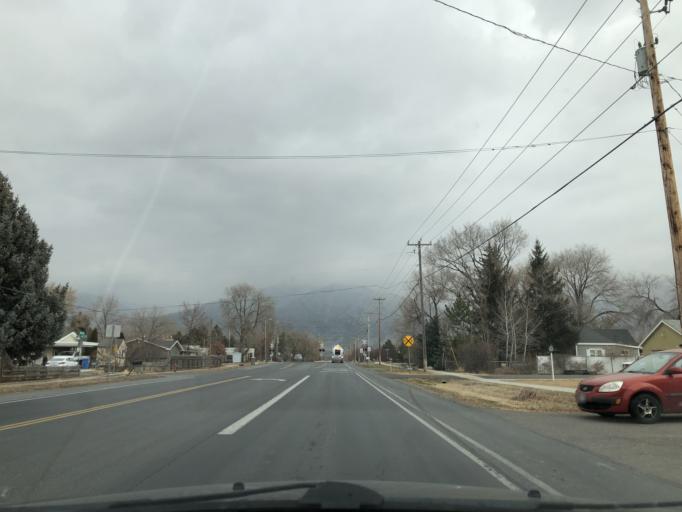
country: US
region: Utah
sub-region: Cache County
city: Nibley
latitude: 41.6749
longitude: -111.8501
